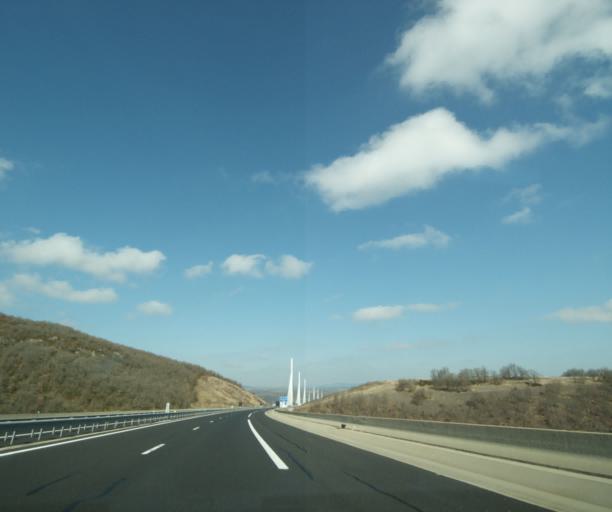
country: FR
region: Midi-Pyrenees
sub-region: Departement de l'Aveyron
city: Saint-Georges-de-Luzencon
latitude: 44.0641
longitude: 3.0262
